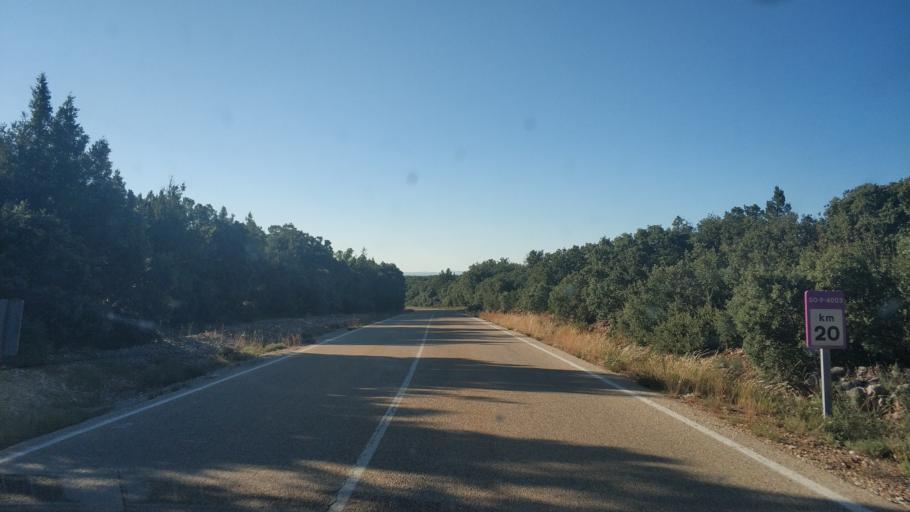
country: ES
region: Castille and Leon
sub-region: Provincia de Soria
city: Montejo de Tiermes
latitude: 41.4122
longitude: -3.2010
